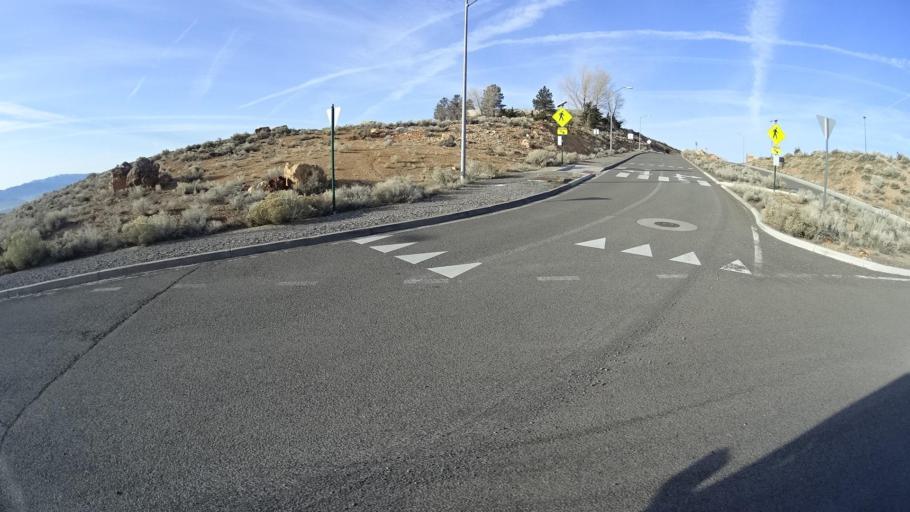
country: US
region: Nevada
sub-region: Washoe County
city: Sun Valley
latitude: 39.5702
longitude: -119.7944
